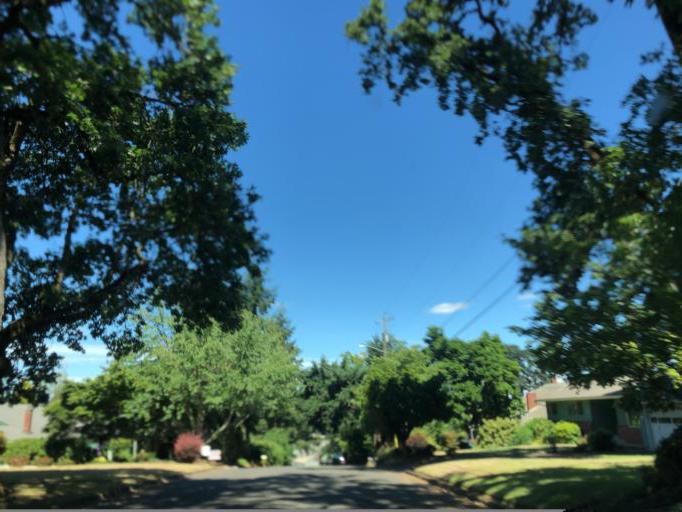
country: US
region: Oregon
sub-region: Marion County
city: Silverton
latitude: 45.0015
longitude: -122.7871
